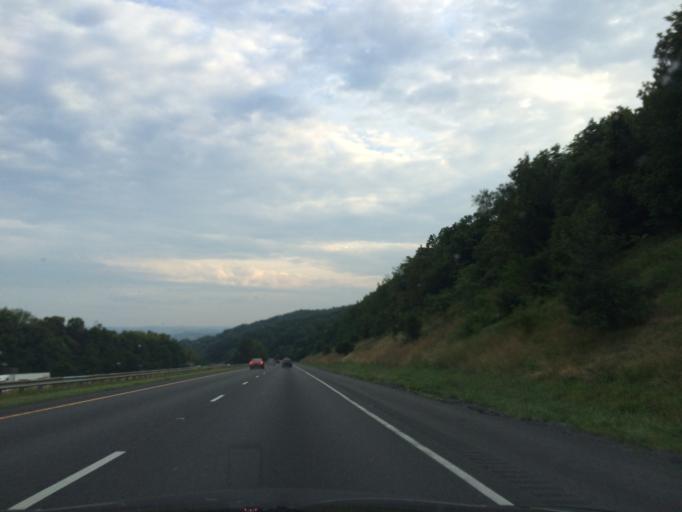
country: US
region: Maryland
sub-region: Frederick County
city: Braddock Heights
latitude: 39.4492
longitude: -77.5035
